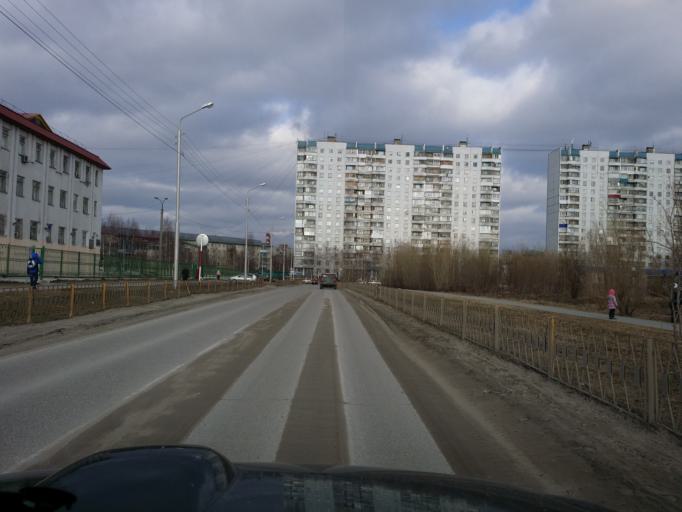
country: RU
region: Khanty-Mansiyskiy Avtonomnyy Okrug
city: Nizhnevartovsk
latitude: 60.9391
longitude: 76.6048
